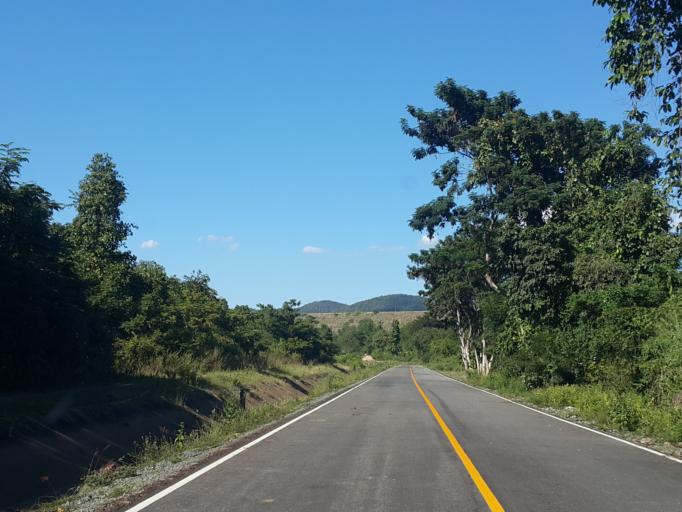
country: TH
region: Chiang Mai
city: San Sai
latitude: 18.9192
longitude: 99.1136
